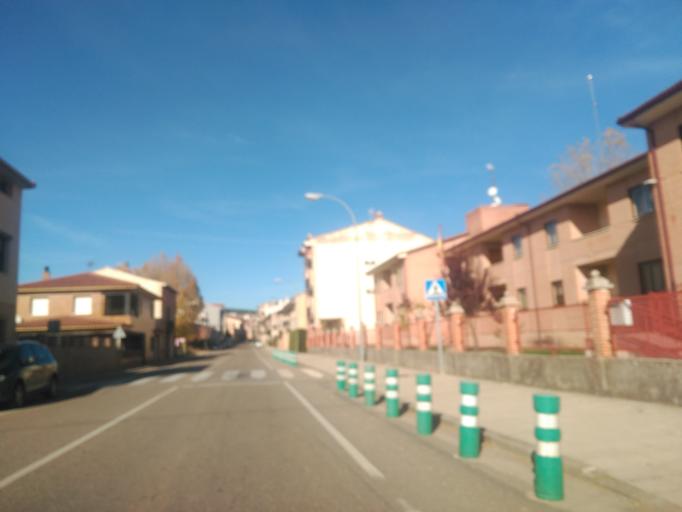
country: ES
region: Castille and Leon
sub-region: Provincia de Burgos
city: Huerta del Rey
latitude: 41.8356
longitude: -3.3461
